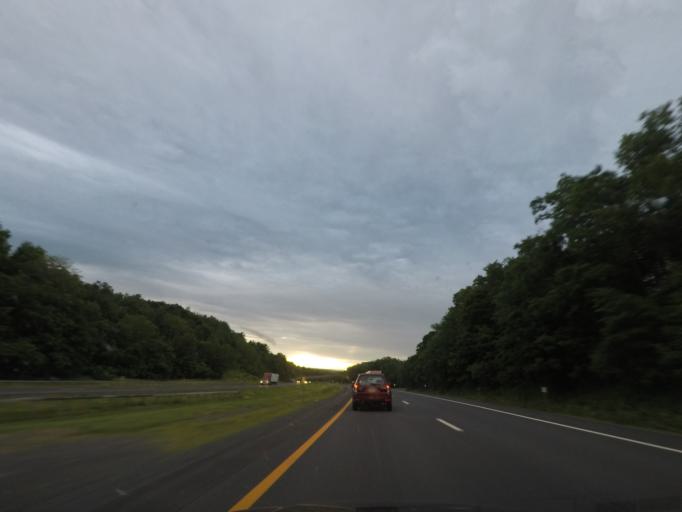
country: US
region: New York
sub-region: Rensselaer County
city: Nassau
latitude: 42.4446
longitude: -73.5602
